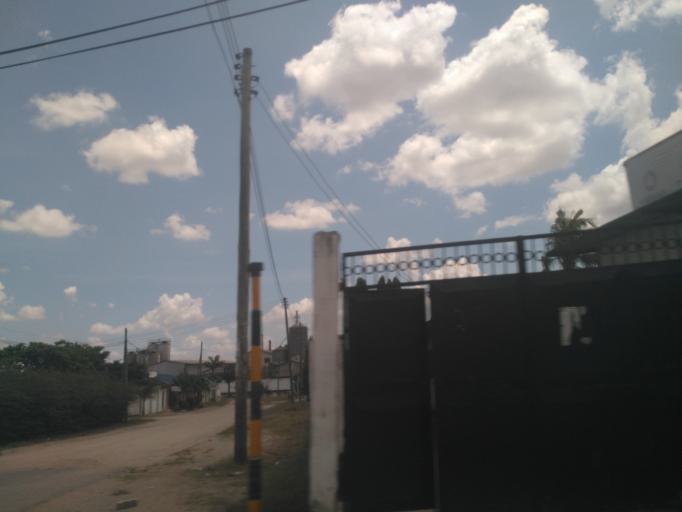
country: TZ
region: Dar es Salaam
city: Dar es Salaam
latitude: -6.8499
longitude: 39.2658
